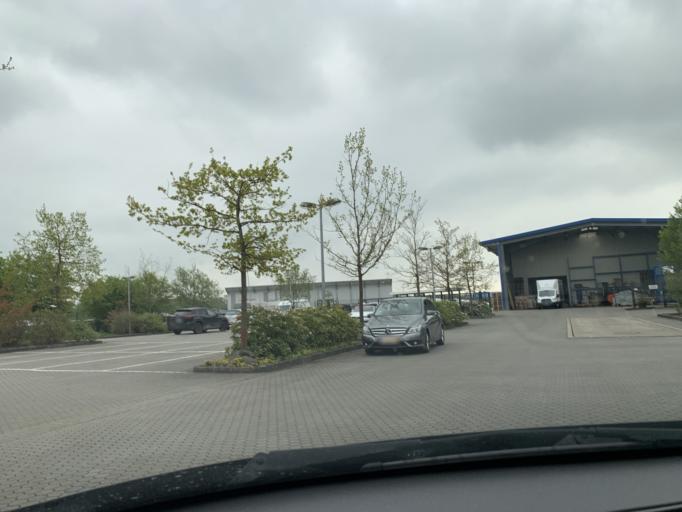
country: DE
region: Lower Saxony
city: Apen
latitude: 53.2459
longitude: 7.7702
